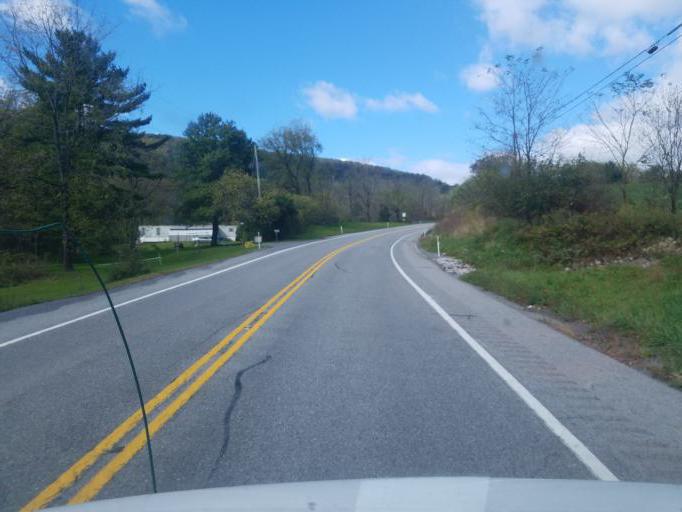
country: US
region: Pennsylvania
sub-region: Fulton County
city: McConnellsburg
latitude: 40.0095
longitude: -78.1086
